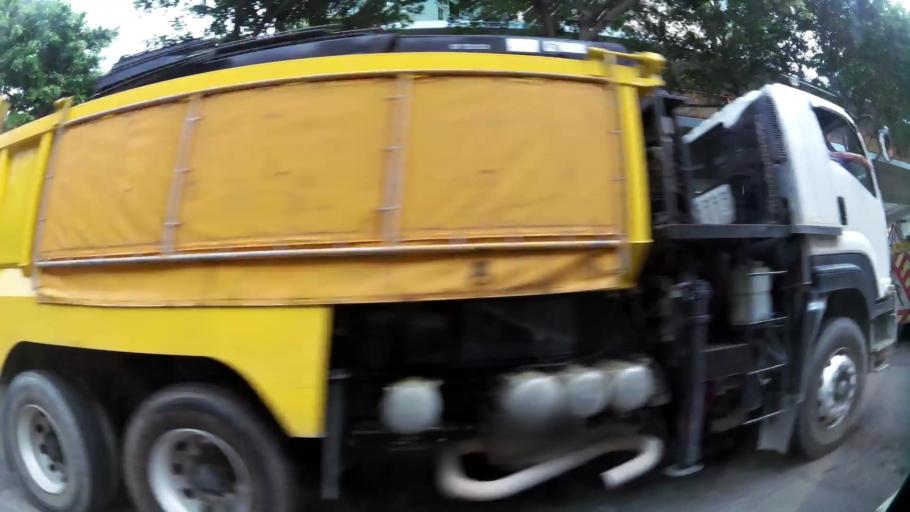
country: HK
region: Kowloon City
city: Kowloon
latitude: 22.3053
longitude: 114.1838
